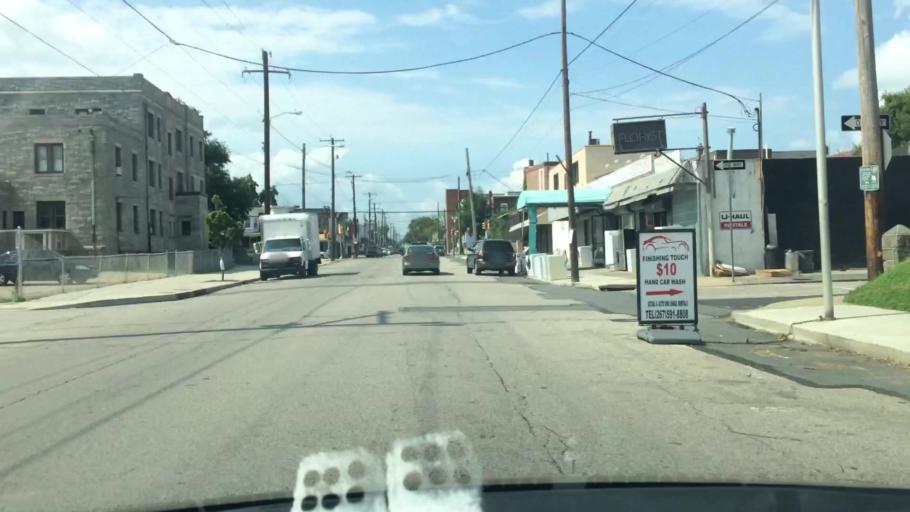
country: US
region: Pennsylvania
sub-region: Delaware County
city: Colwyn
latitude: 39.9222
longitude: -75.2255
